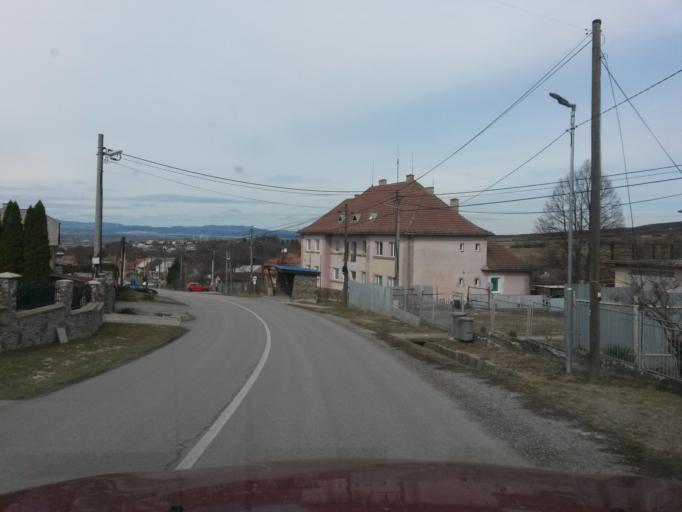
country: HU
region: Borsod-Abauj-Zemplen
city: Gonc
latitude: 48.5830
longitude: 21.3856
